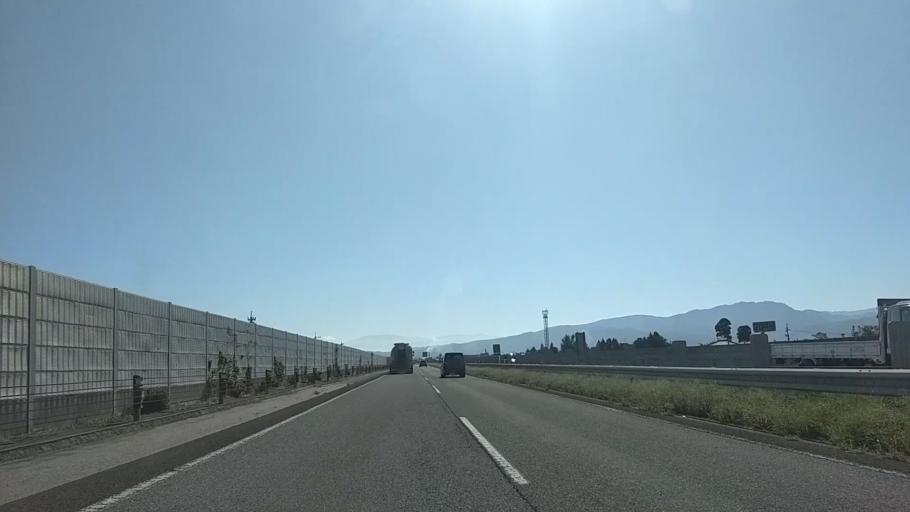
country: JP
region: Toyama
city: Nanto-shi
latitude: 36.6262
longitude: 136.9258
